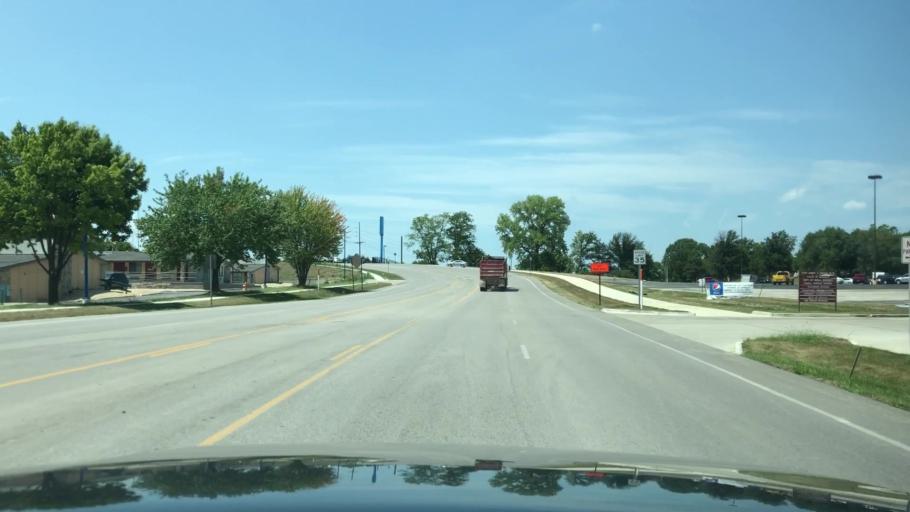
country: US
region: Missouri
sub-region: Saint Charles County
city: Saint Peters
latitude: 38.7964
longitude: -90.5621
